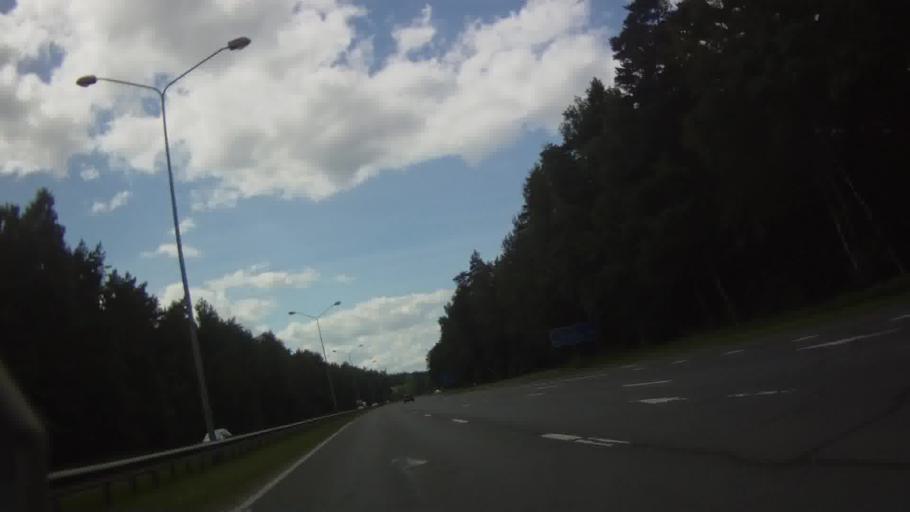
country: LV
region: Babite
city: Pinki
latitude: 56.9496
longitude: 23.9494
